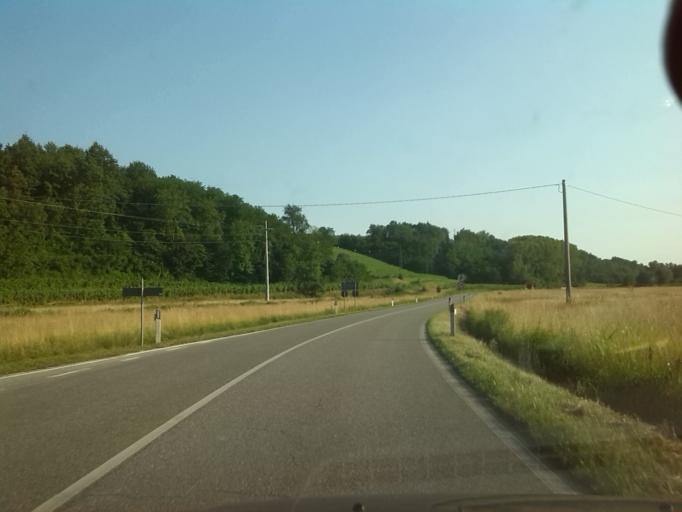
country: IT
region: Friuli Venezia Giulia
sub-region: Provincia di Gorizia
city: Dolegna del Collio
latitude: 46.0186
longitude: 13.4780
